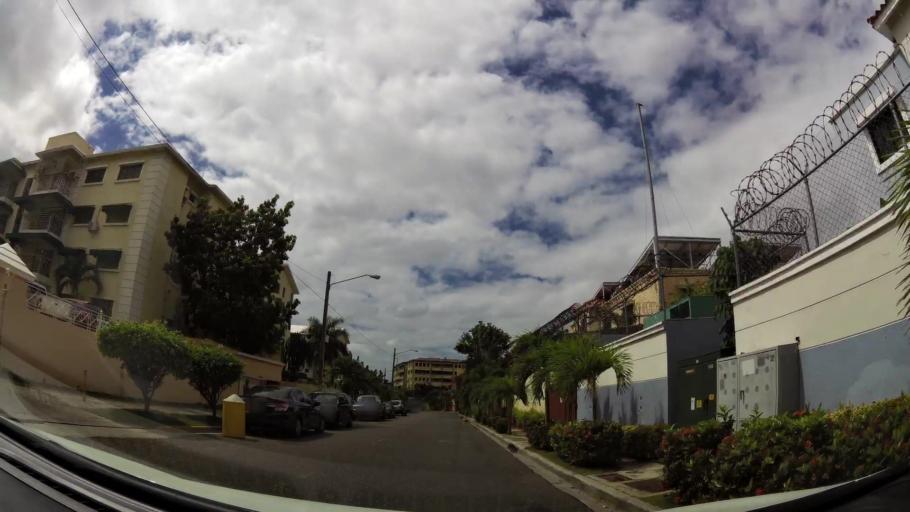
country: DO
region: Nacional
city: Bella Vista
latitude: 18.4656
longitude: -69.9652
